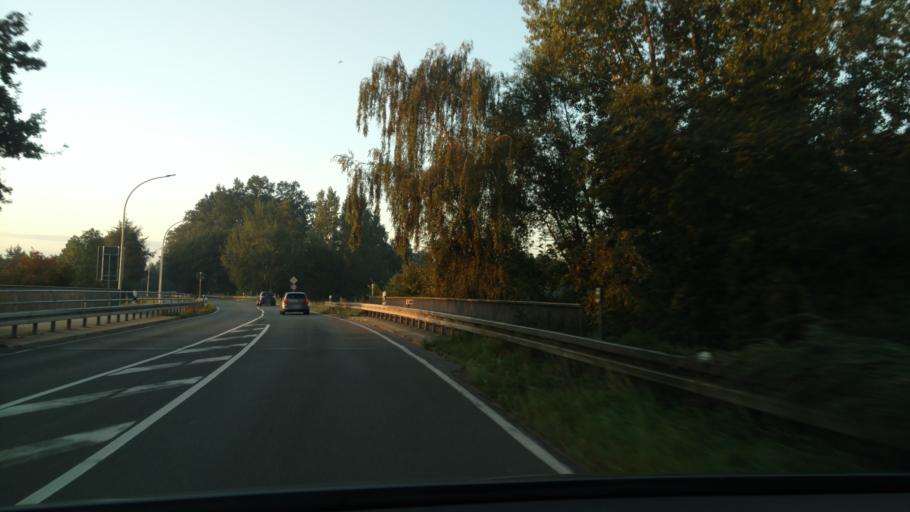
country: DE
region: North Rhine-Westphalia
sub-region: Regierungsbezirk Munster
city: Borken
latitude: 51.8571
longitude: 6.8414
